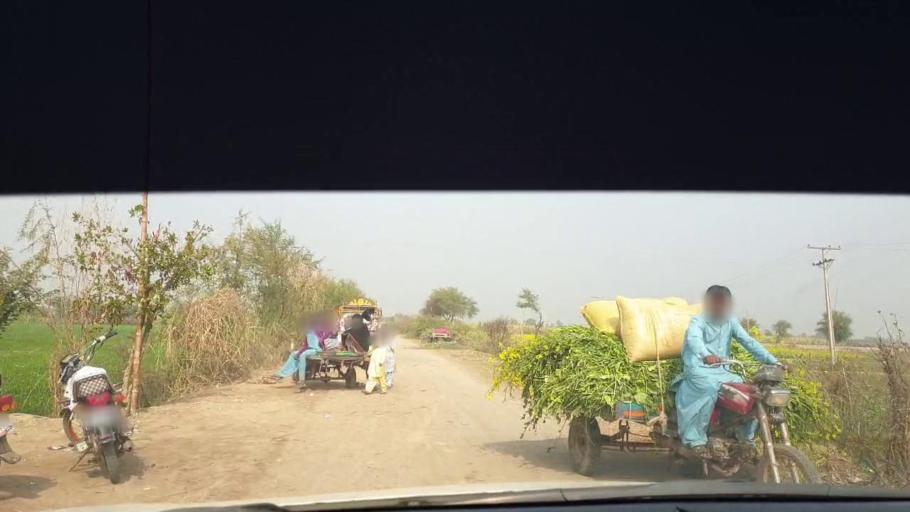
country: PK
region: Sindh
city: Berani
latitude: 25.8054
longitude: 68.8363
